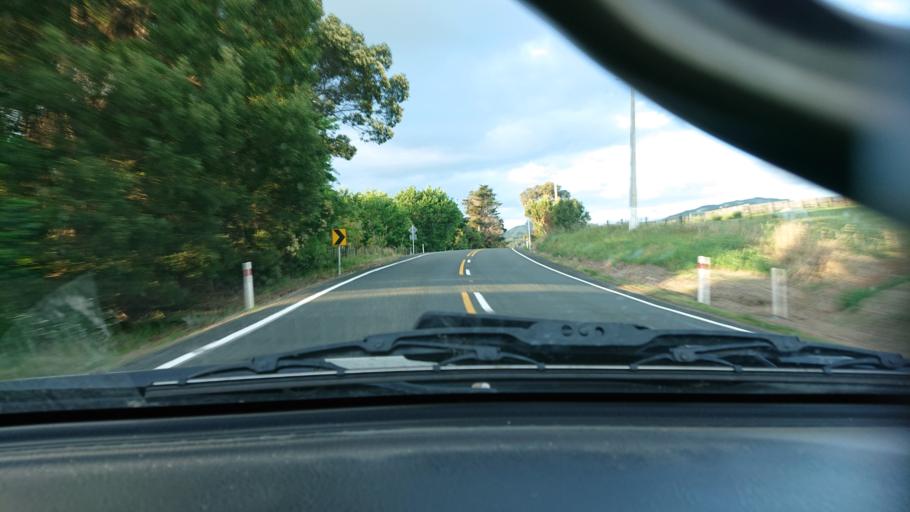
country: NZ
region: Auckland
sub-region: Auckland
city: Parakai
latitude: -36.5211
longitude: 174.4487
